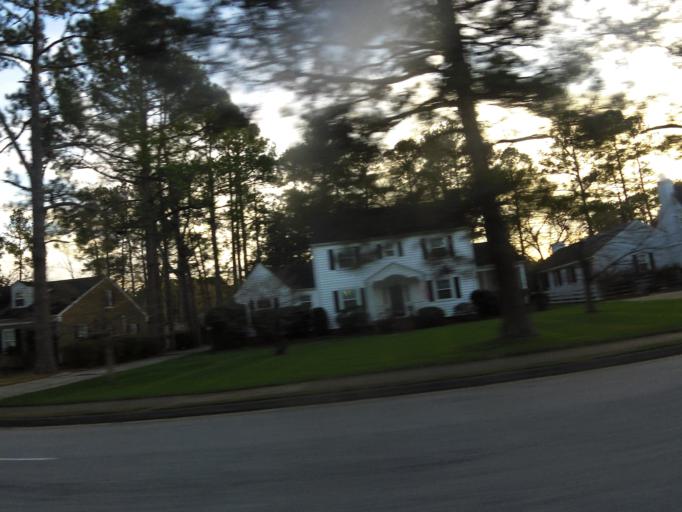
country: US
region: Virginia
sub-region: City of Franklin
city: Franklin
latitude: 36.6829
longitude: -76.9387
